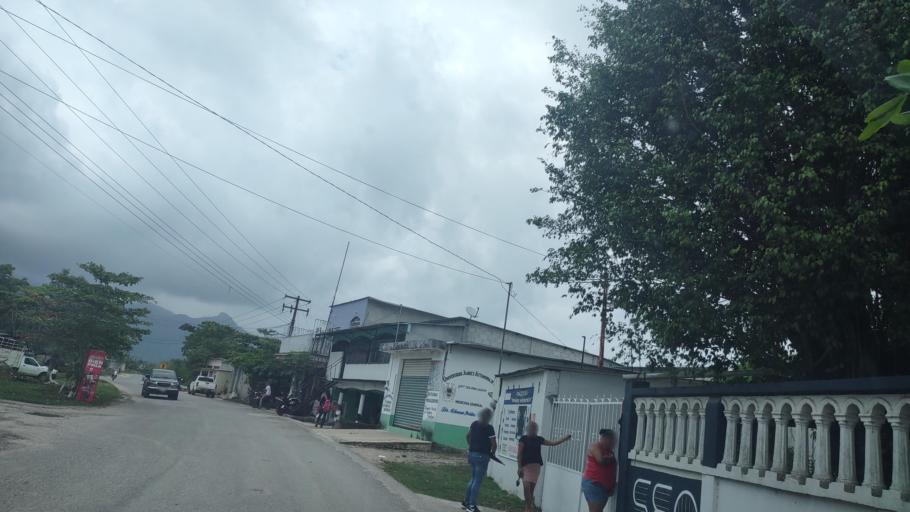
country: MX
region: Veracruz
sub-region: Uxpanapa
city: Poblado 10
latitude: 17.4994
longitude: -94.1629
